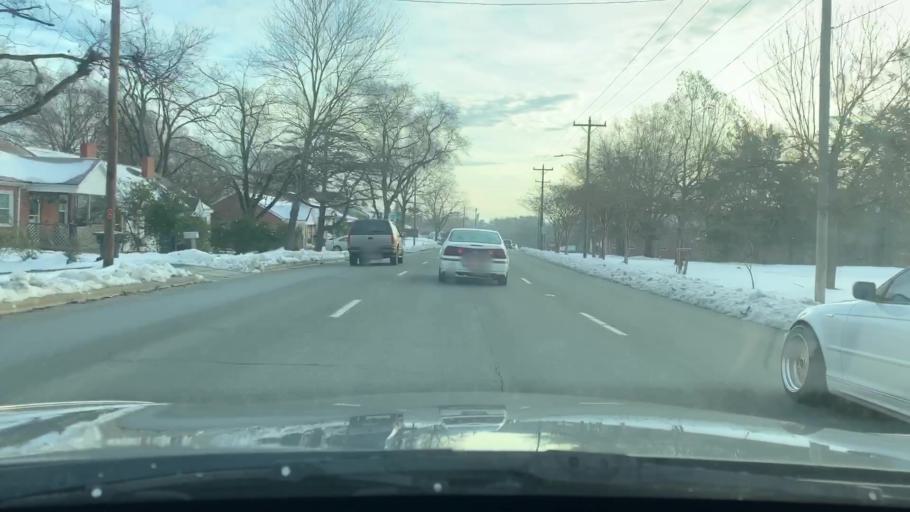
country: US
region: North Carolina
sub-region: Alamance County
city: Burlington
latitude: 36.1017
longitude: -79.4284
